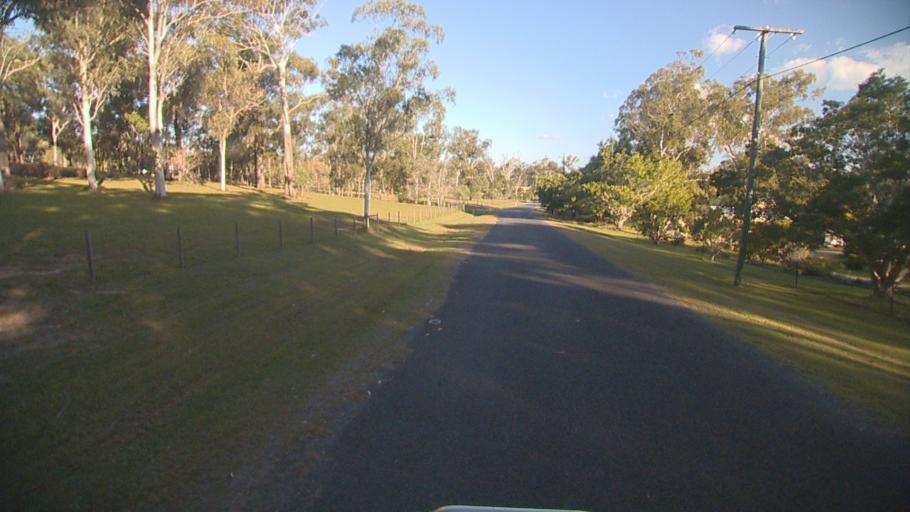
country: AU
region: Queensland
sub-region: Redland
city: Redland Bay
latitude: -27.6579
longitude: 153.2671
